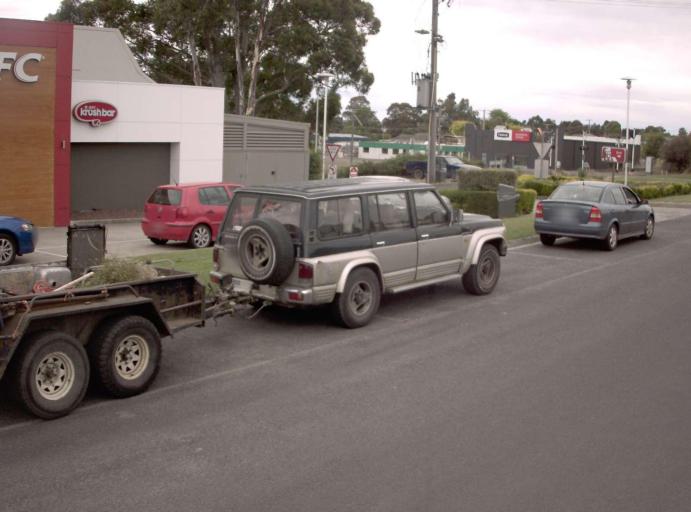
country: AU
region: Victoria
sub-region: Baw Baw
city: Warragul
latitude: -38.4723
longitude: 145.9432
